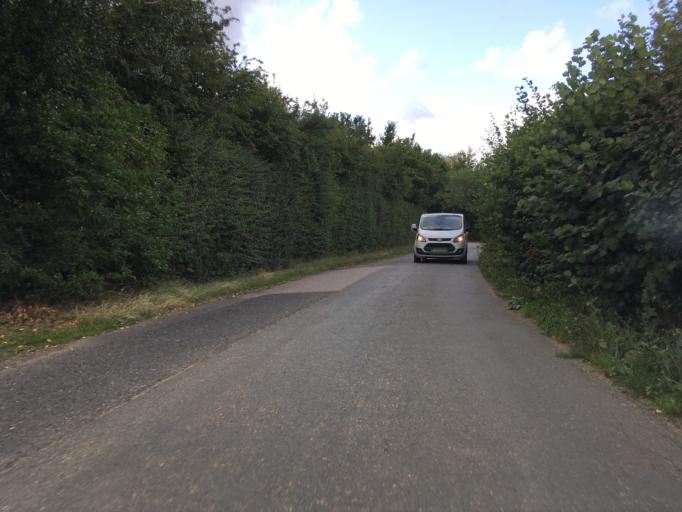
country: GB
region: England
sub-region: Kent
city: Maidstone
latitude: 51.2305
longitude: 0.5398
